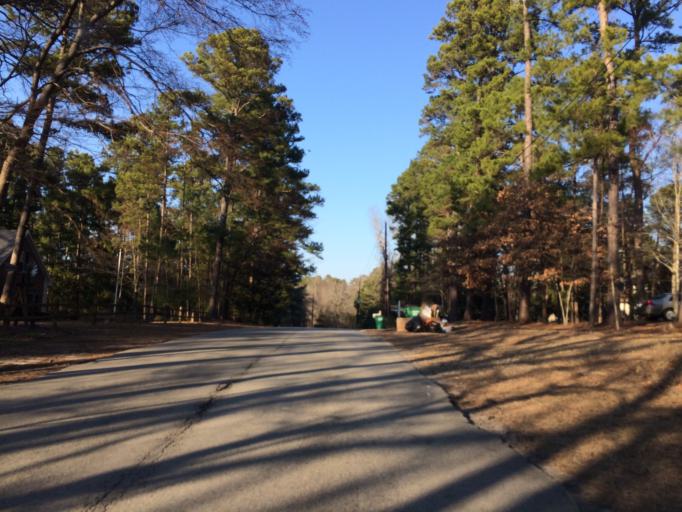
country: US
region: Texas
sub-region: Wood County
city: Hawkins
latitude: 32.7137
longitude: -95.1805
